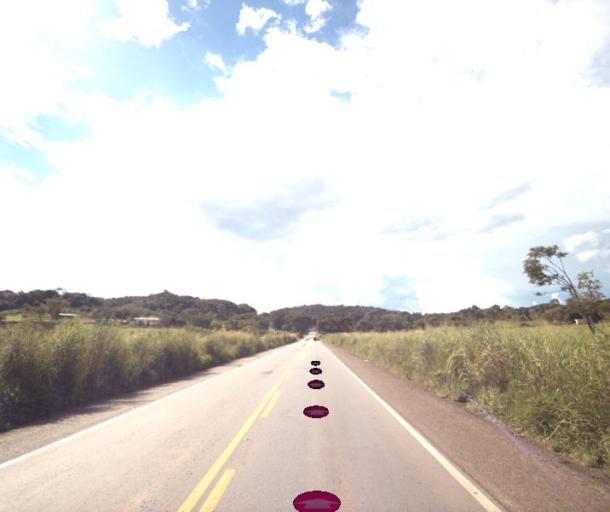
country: BR
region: Goias
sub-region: Jaragua
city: Jaragua
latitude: -15.7092
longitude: -49.3308
